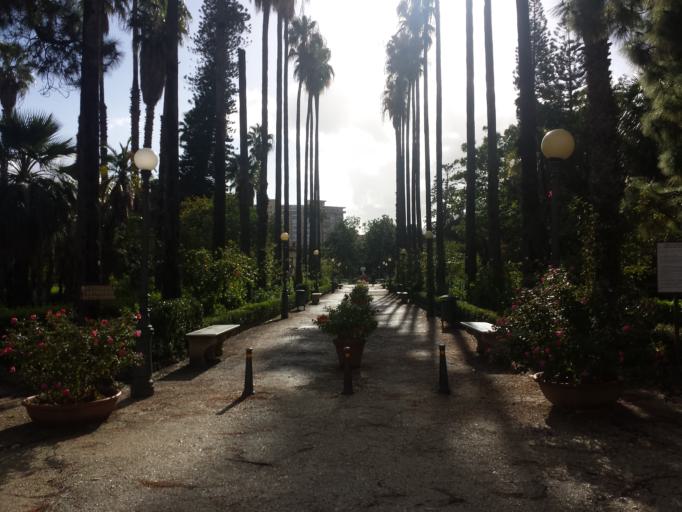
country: IT
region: Sicily
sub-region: Palermo
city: Palermo
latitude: 38.1143
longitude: 13.3750
